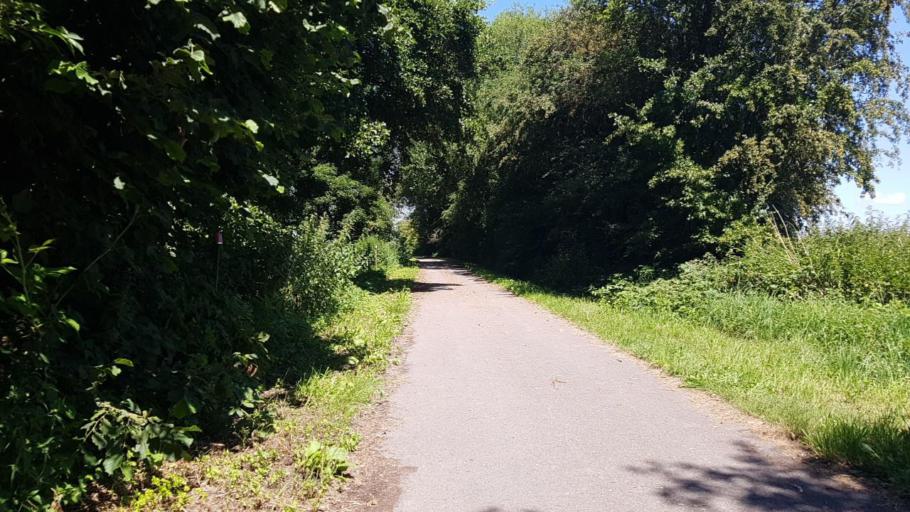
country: BE
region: Wallonia
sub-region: Province du Hainaut
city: Thuin
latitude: 50.2884
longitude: 4.3288
